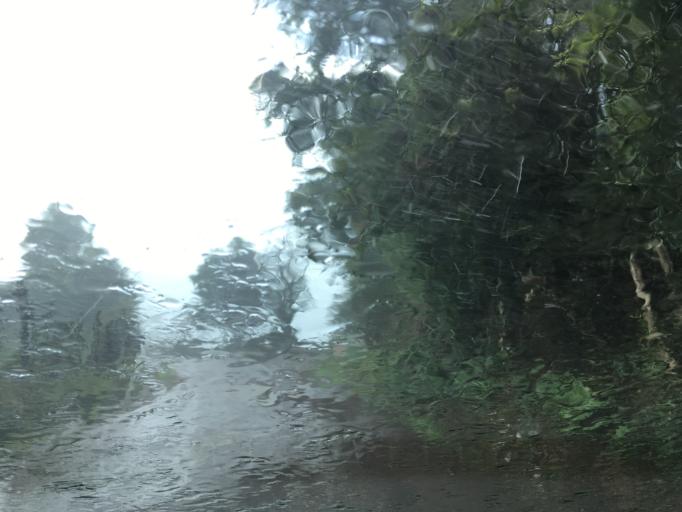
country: MX
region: Michoacan
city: Acuitzio del Canje
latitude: 19.5258
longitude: -101.2230
